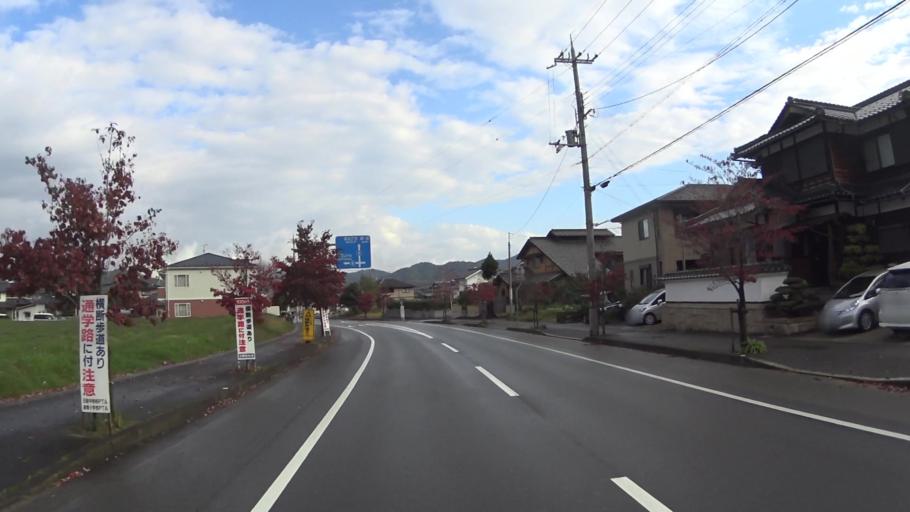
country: JP
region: Kyoto
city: Fukuchiyama
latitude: 35.2980
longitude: 135.1795
